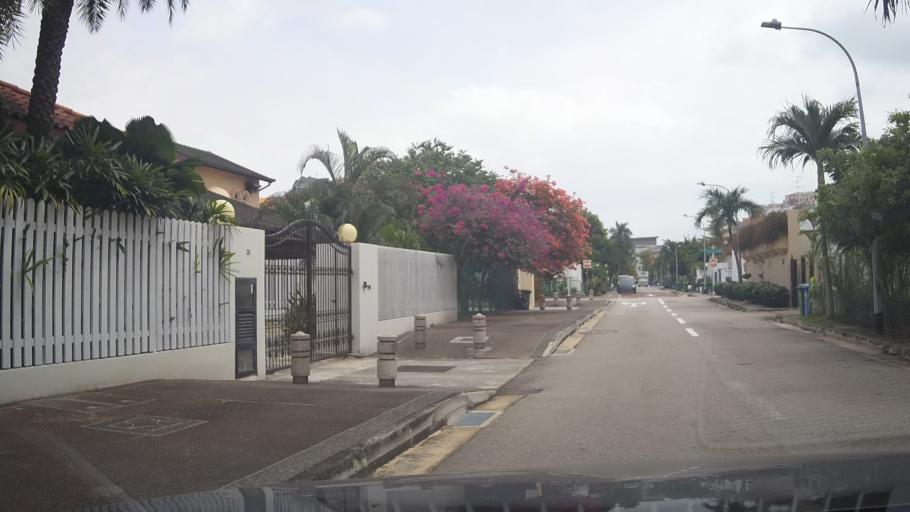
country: SG
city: Singapore
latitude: 1.3071
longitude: 103.8923
